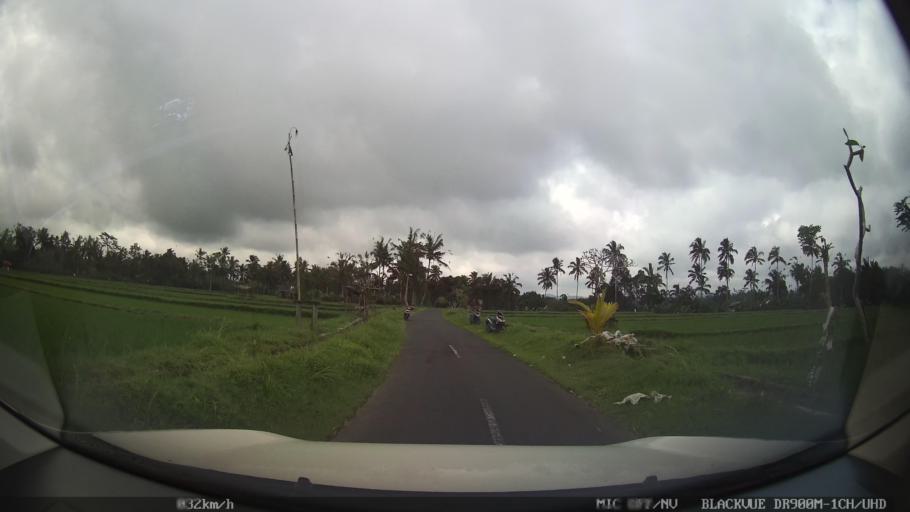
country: ID
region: Bali
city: Badung
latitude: -8.4186
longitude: 115.2269
